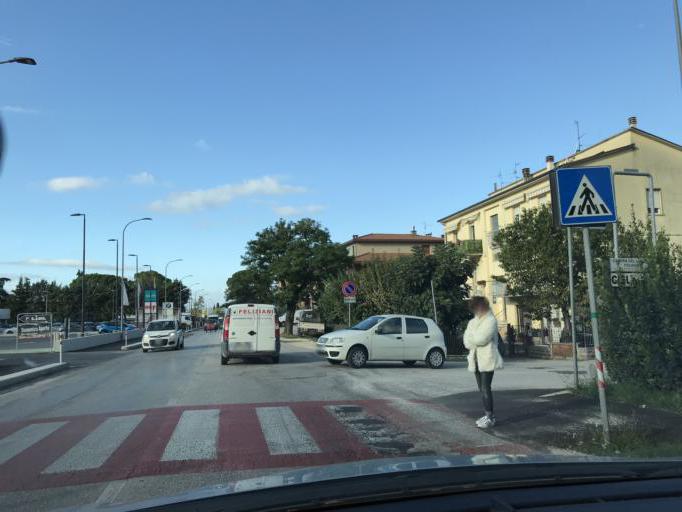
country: IT
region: Umbria
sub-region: Provincia di Perugia
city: Foligno
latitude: 42.9651
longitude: 12.6905
